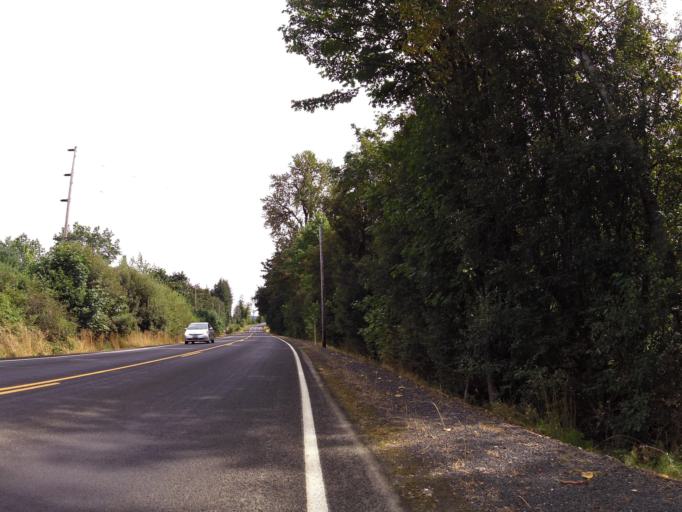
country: US
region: Washington
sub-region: Cowlitz County
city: Castle Rock
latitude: 46.3358
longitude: -122.9349
